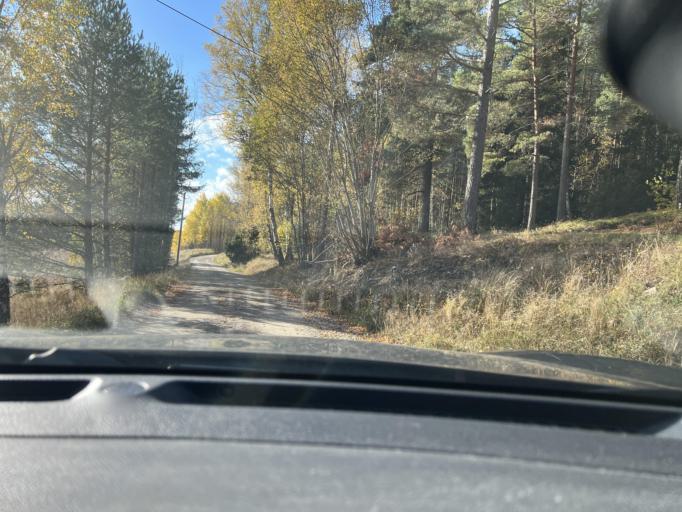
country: SE
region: Stockholm
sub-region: Vallentuna Kommun
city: Vallentuna
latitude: 59.5100
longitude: 18.1078
